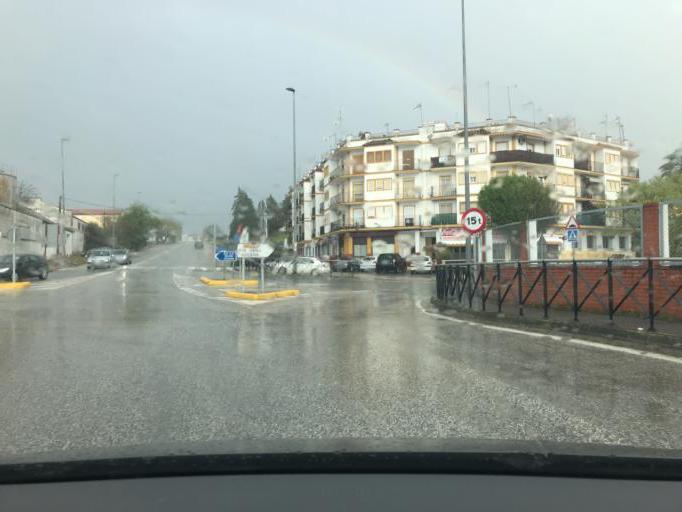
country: ES
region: Andalusia
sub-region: Provincia de Sevilla
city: Ecija
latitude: 37.5441
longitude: -5.0704
